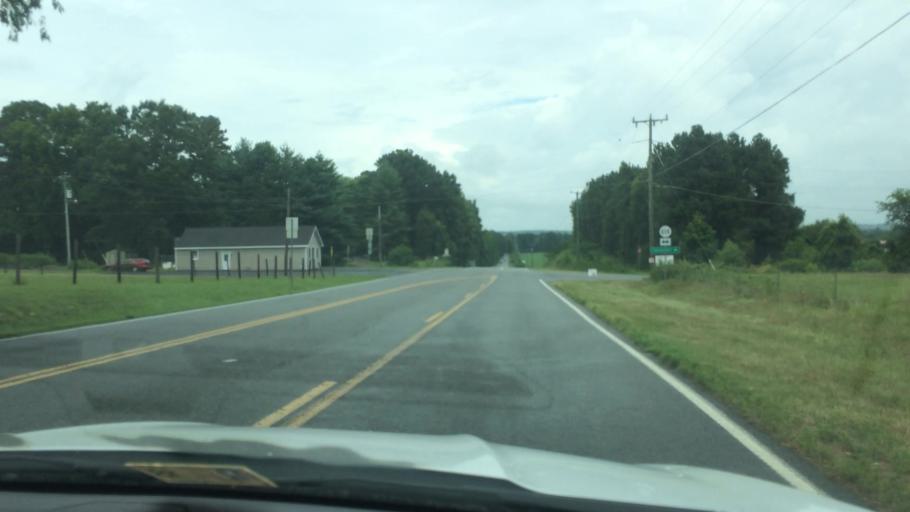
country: US
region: Virginia
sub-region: Charles City County
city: Charles City
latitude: 37.4127
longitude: -77.0449
